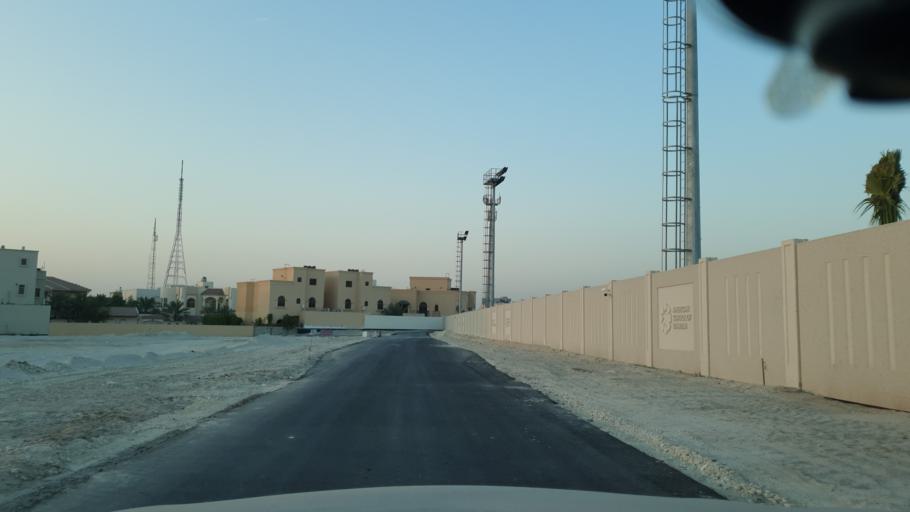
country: BH
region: Northern
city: Madinat `Isa
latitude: 26.1563
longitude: 50.5598
